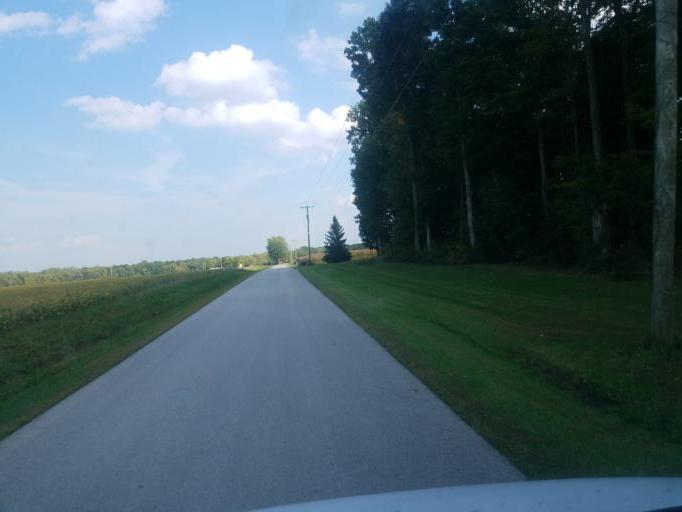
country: US
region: Ohio
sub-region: Hancock County
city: Arlington
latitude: 40.8769
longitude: -83.5748
